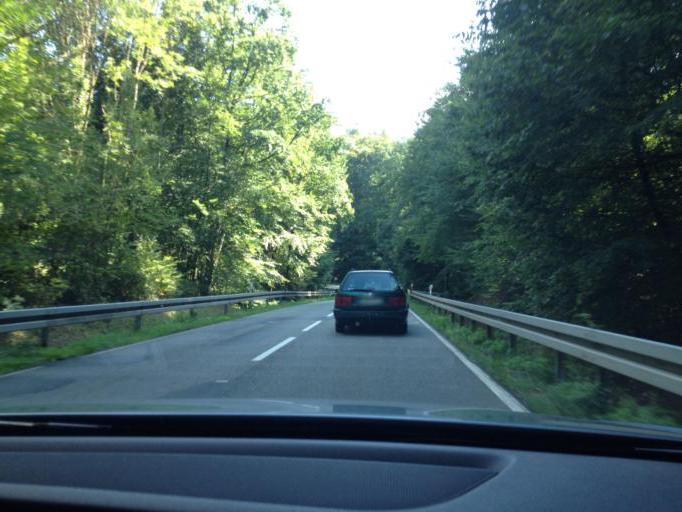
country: DE
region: Saarland
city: Marpingen
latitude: 49.4179
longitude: 7.0737
